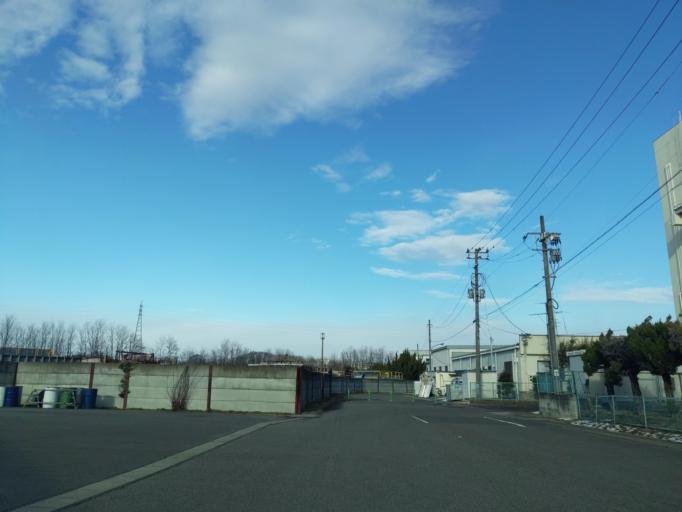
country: JP
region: Fukushima
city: Motomiya
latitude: 37.4730
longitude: 140.3759
